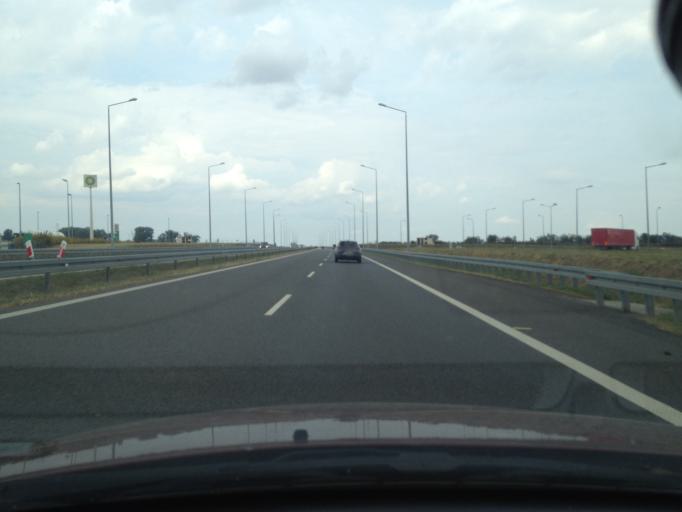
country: PL
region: West Pomeranian Voivodeship
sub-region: Powiat pyrzycki
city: Kozielice
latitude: 53.0512
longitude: 14.8658
